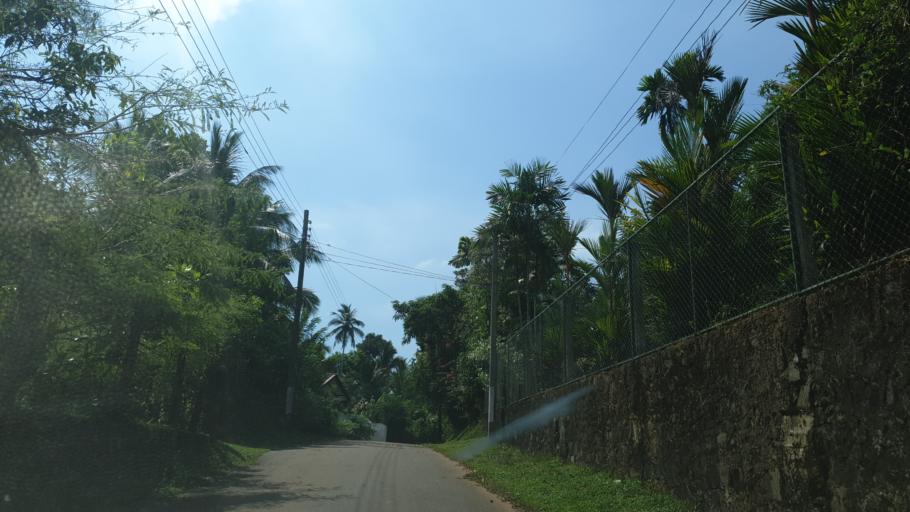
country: LK
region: Western
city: Panadura
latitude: 6.7239
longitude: 79.9648
